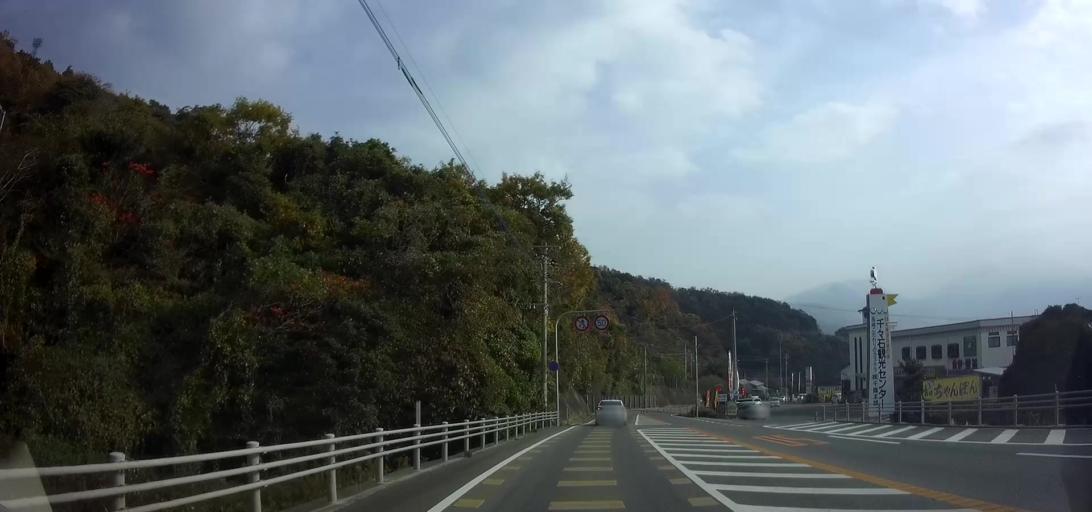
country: JP
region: Nagasaki
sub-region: Isahaya-shi
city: Isahaya
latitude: 32.7959
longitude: 130.1753
